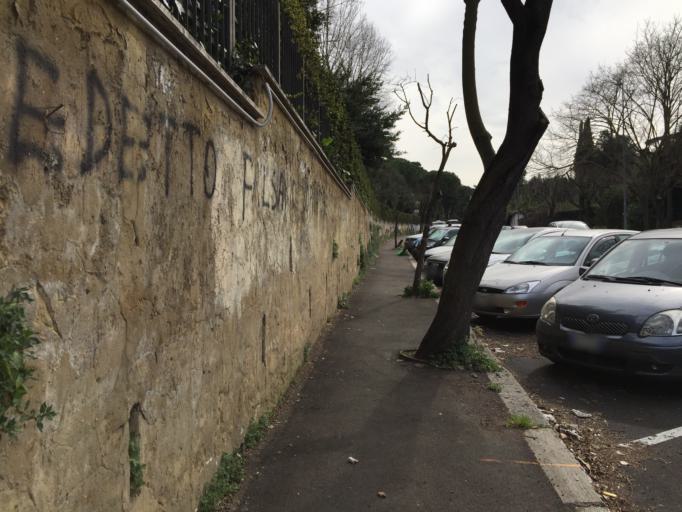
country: VA
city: Vatican City
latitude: 41.8927
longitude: 12.4586
